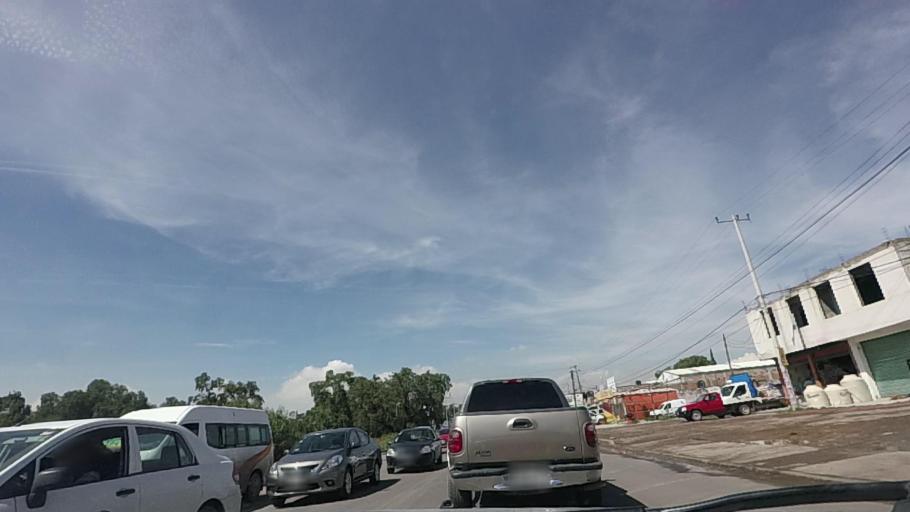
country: MX
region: Mexico
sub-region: Cuautitlan
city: Barrio Tlatenco
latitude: 19.7293
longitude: -99.1865
